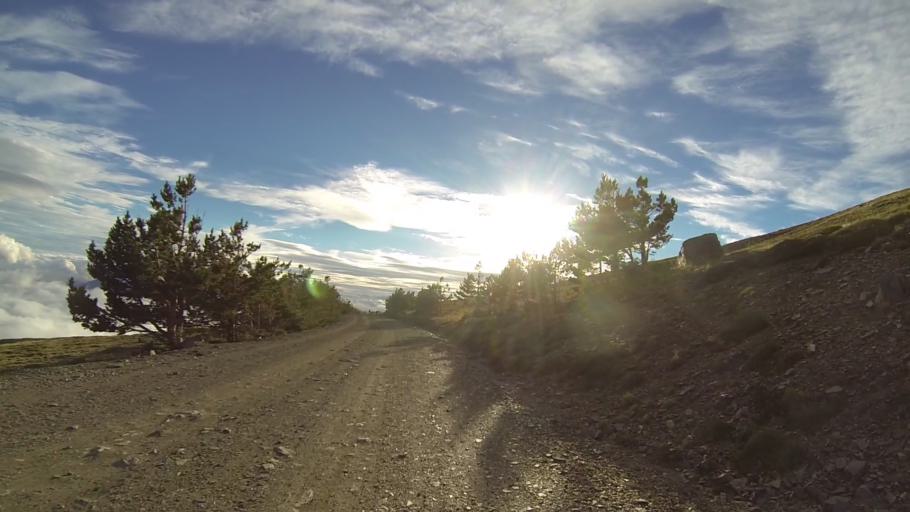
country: ES
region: Andalusia
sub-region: Provincia de Granada
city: Portugos
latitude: 36.9828
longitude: -3.3196
